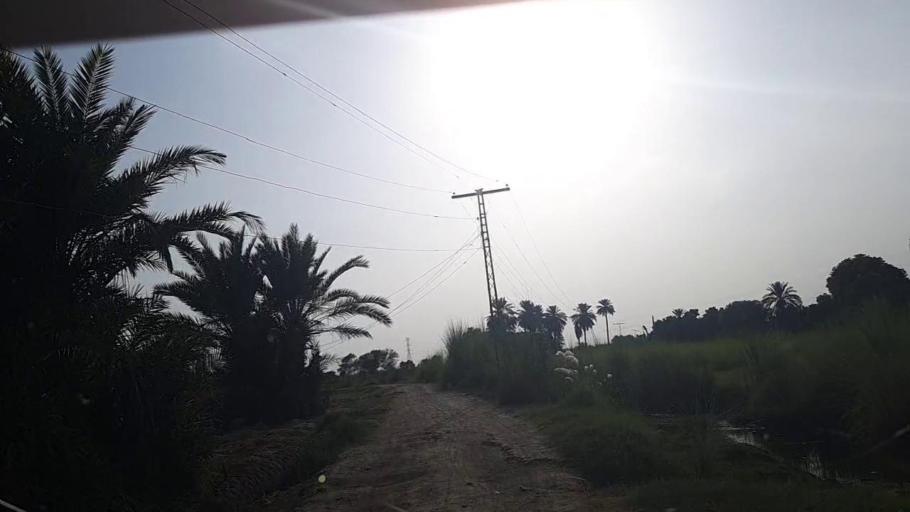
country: PK
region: Sindh
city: Ghotki
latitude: 27.9778
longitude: 69.2586
